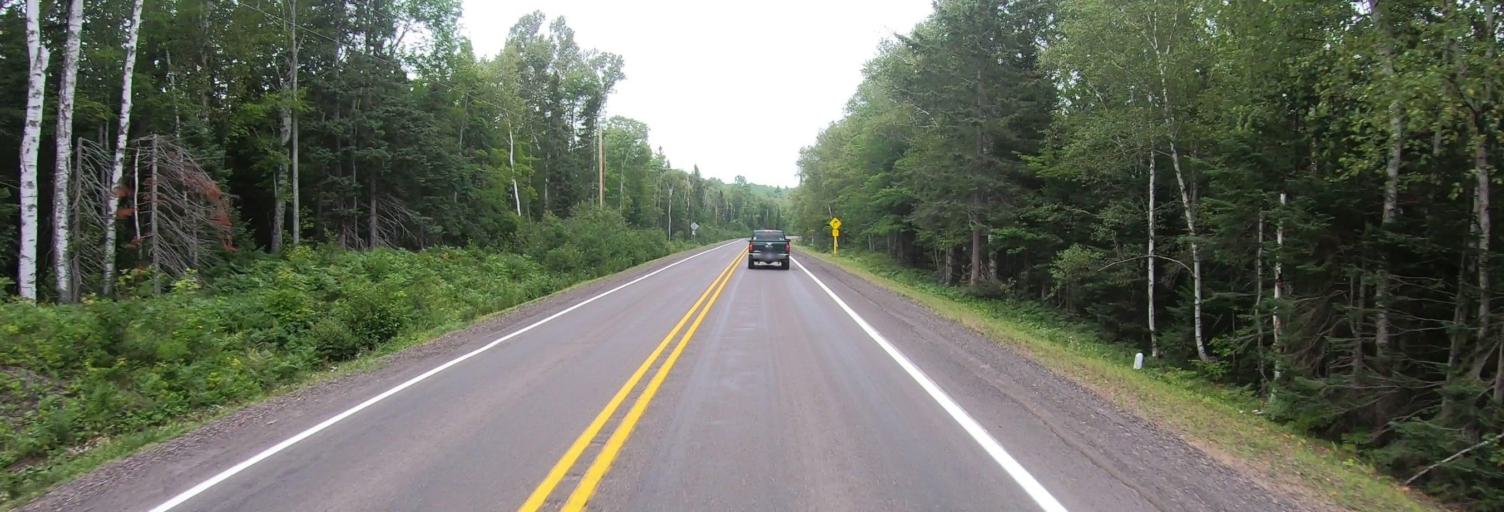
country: US
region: Michigan
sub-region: Keweenaw County
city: Eagle River
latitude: 47.4164
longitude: -88.1383
